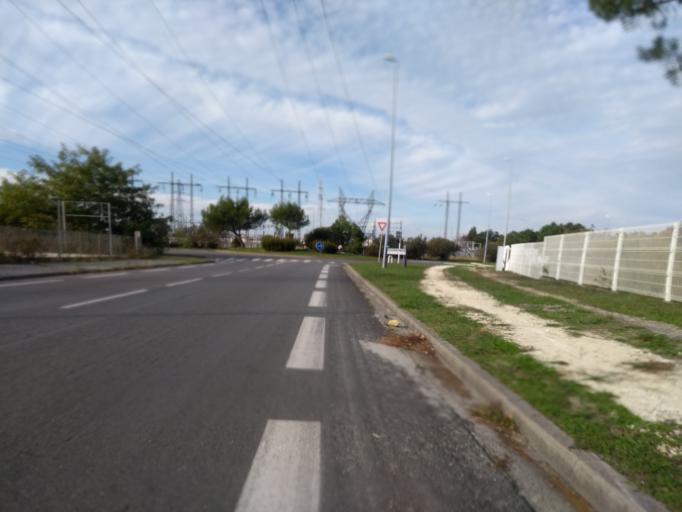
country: FR
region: Aquitaine
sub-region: Departement de la Gironde
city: Pessac
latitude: 44.7861
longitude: -0.6644
